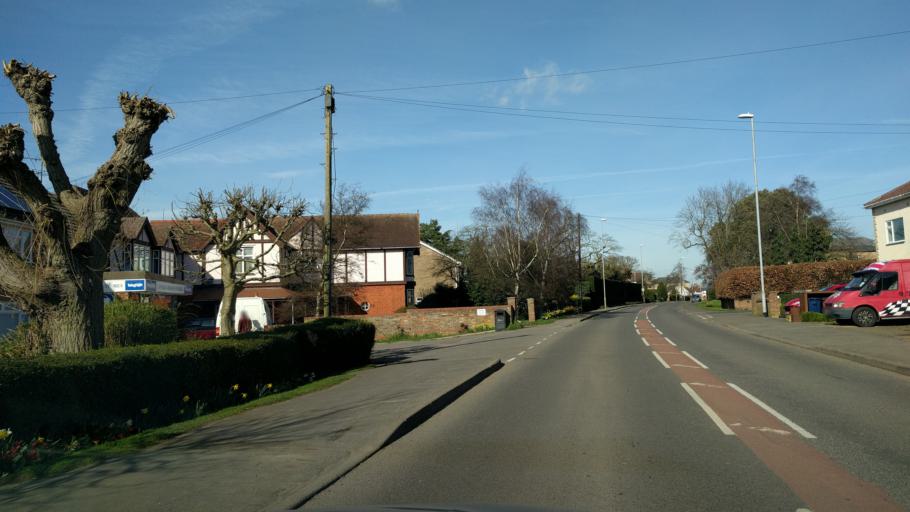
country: GB
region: England
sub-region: Cambridgeshire
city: Chatteris
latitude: 52.4454
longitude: 0.0457
